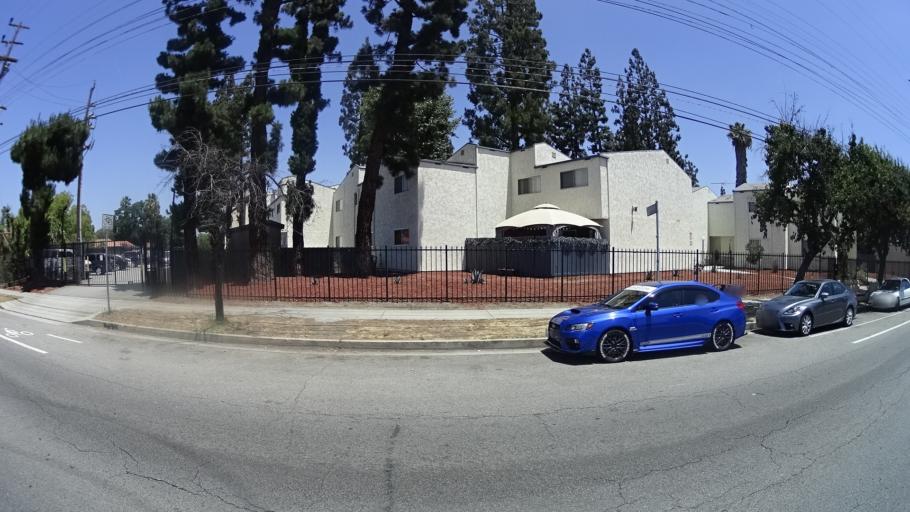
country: US
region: California
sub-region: Los Angeles County
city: San Fernando
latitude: 34.2354
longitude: -118.4419
